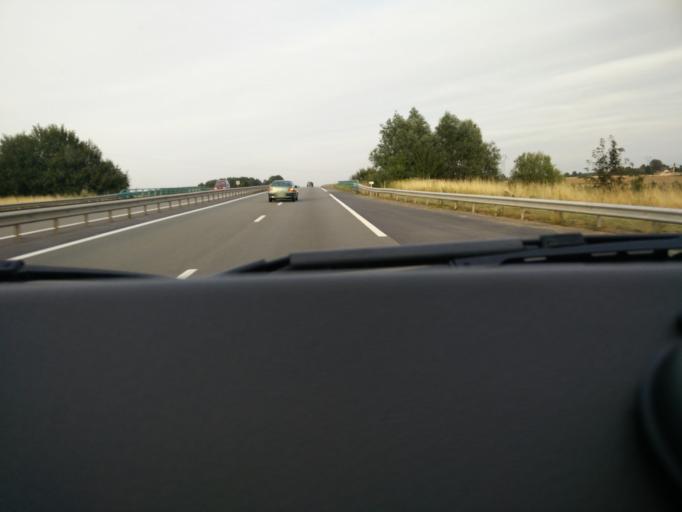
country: FR
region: Nord-Pas-de-Calais
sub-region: Departement du Nord
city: Wargnies-le-Grand
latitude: 50.3015
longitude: 3.6774
